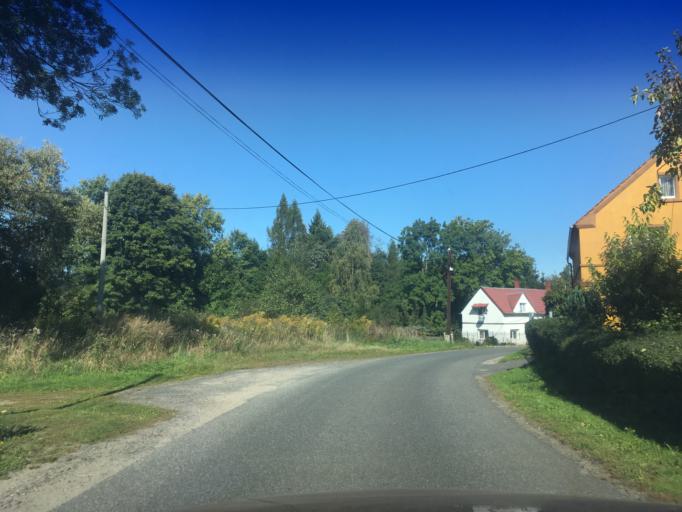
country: PL
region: Lower Silesian Voivodeship
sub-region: Powiat lubanski
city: Lesna
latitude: 51.0081
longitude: 15.1937
